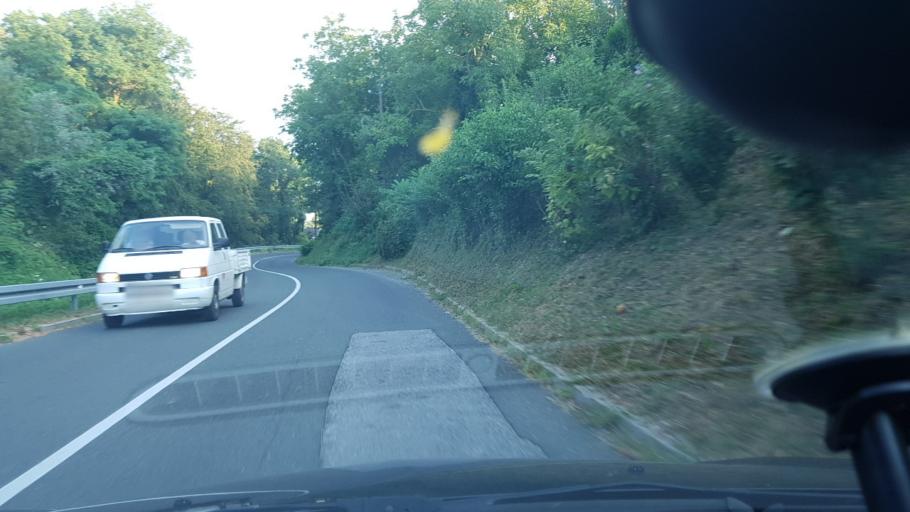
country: HR
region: Krapinsko-Zagorska
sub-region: Grad Krapina
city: Krapina
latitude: 46.1636
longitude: 15.8577
